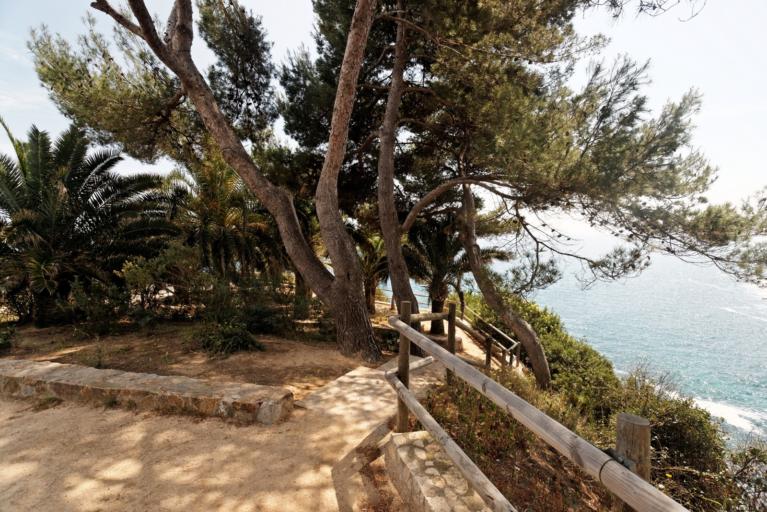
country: ES
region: Catalonia
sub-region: Provincia de Girona
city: Lloret de Mar
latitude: 41.6955
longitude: 2.8445
